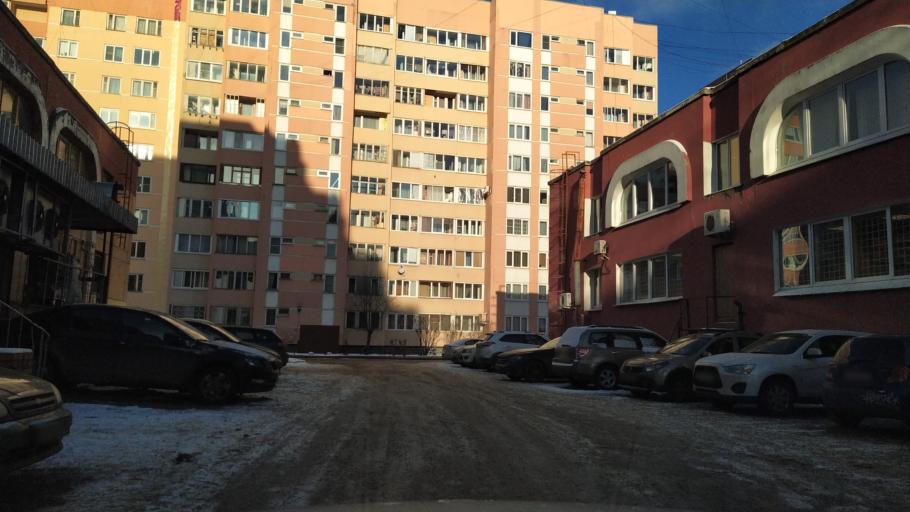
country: RU
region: Leningrad
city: Untolovo
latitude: 59.9886
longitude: 30.2173
